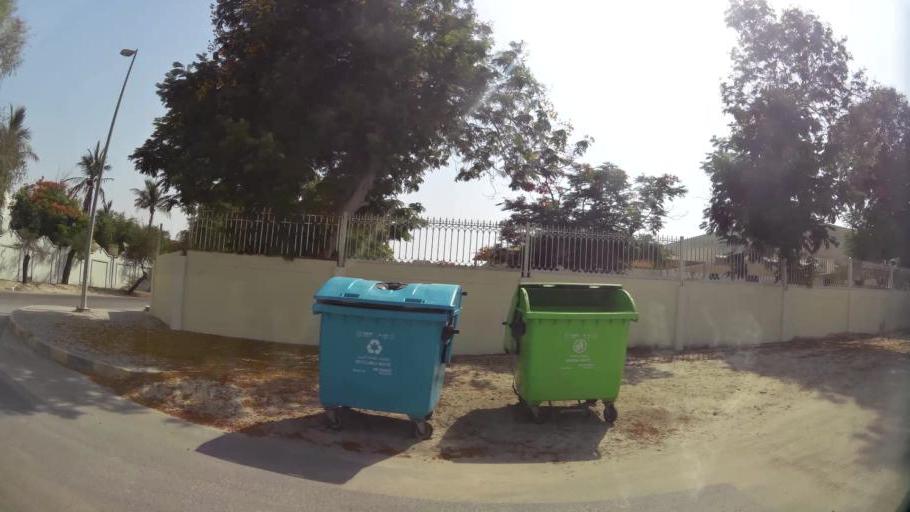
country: AE
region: Ajman
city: Ajman
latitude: 25.3838
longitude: 55.4182
